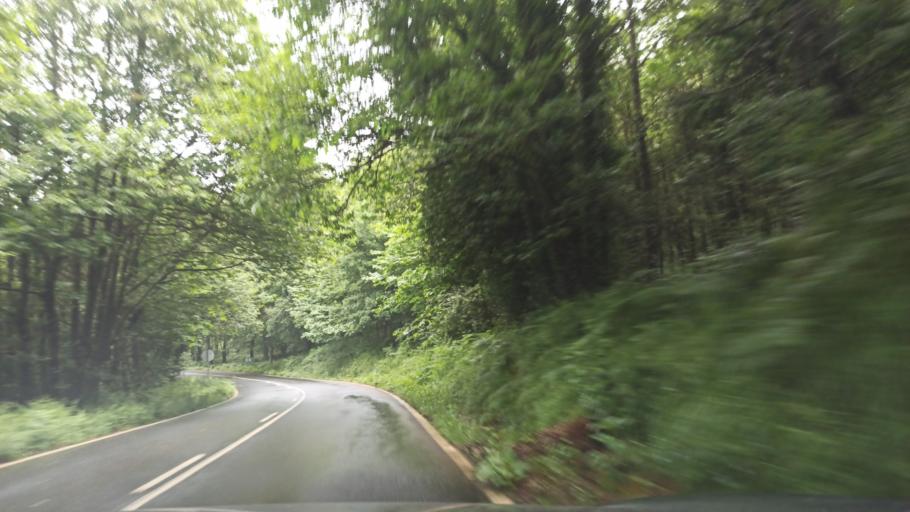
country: ES
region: Galicia
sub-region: Provincia da Coruna
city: Santiso
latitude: 42.7834
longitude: -8.0803
